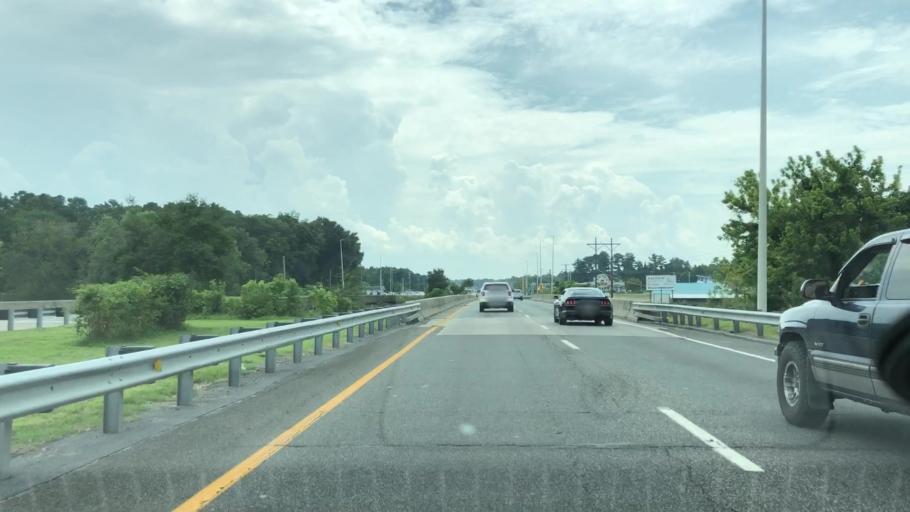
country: US
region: Delaware
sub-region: Sussex County
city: Seaford
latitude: 38.6440
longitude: -75.5942
